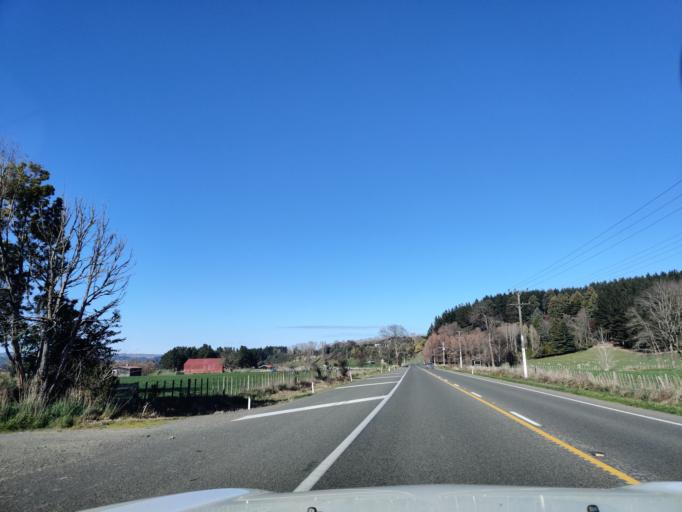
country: NZ
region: Manawatu-Wanganui
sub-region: Rangitikei District
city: Bulls
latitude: -39.9146
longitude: 175.6352
